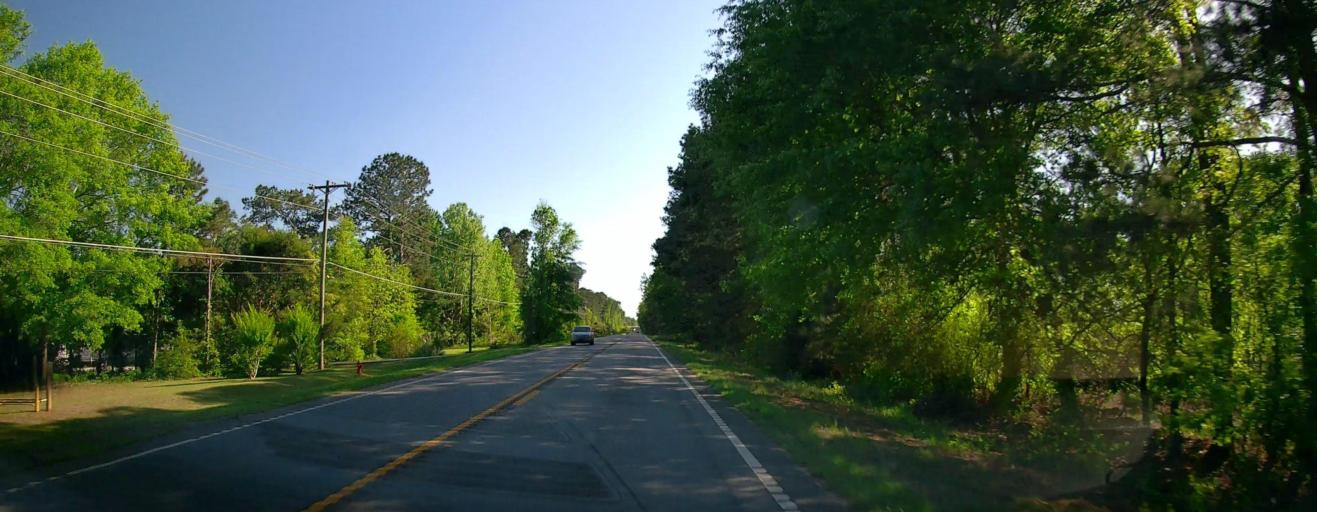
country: US
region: Georgia
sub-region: Houston County
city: Robins Air Force Base
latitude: 32.5160
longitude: -83.5984
